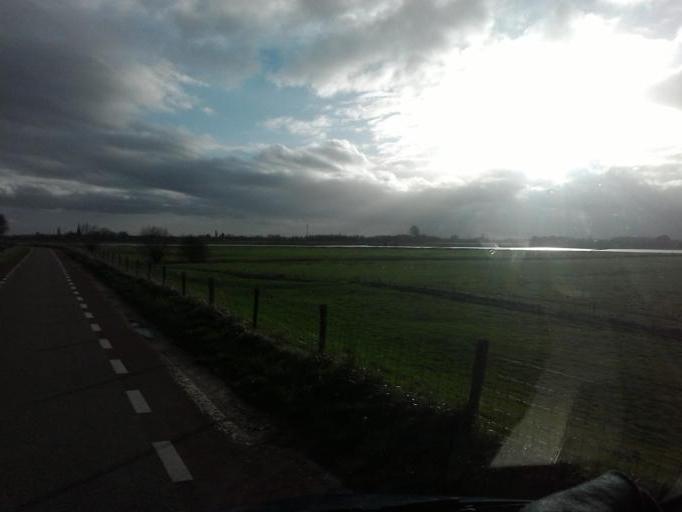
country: NL
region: Utrecht
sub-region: Gemeente Houten
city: Houten
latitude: 51.9768
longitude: 5.1535
